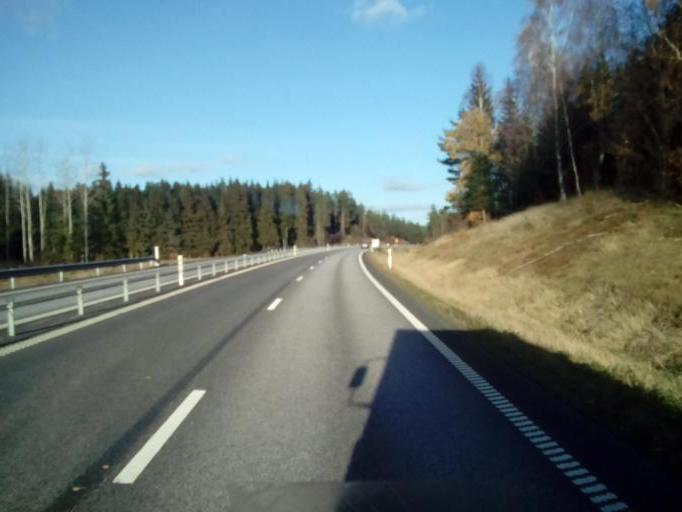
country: SE
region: Kalmar
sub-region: Vimmerby Kommun
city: Vimmerby
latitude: 57.7028
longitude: 16.0191
